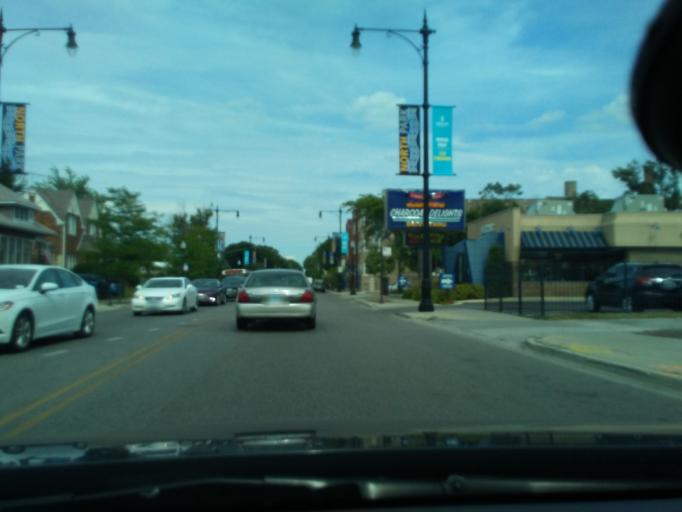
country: US
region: Illinois
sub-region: Cook County
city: Lincolnwood
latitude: 41.9757
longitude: -87.7082
